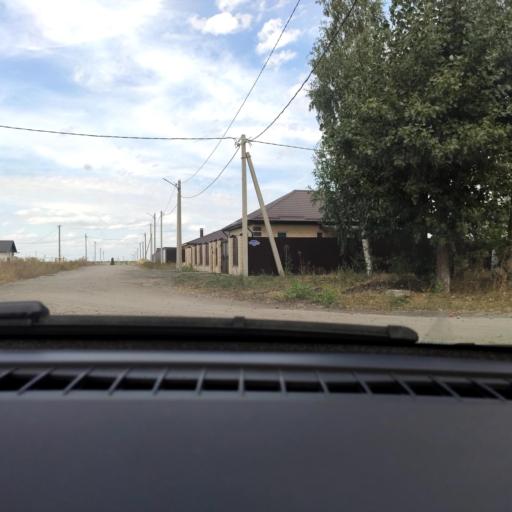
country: RU
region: Voronezj
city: Novaya Usman'
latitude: 51.6684
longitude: 39.4381
